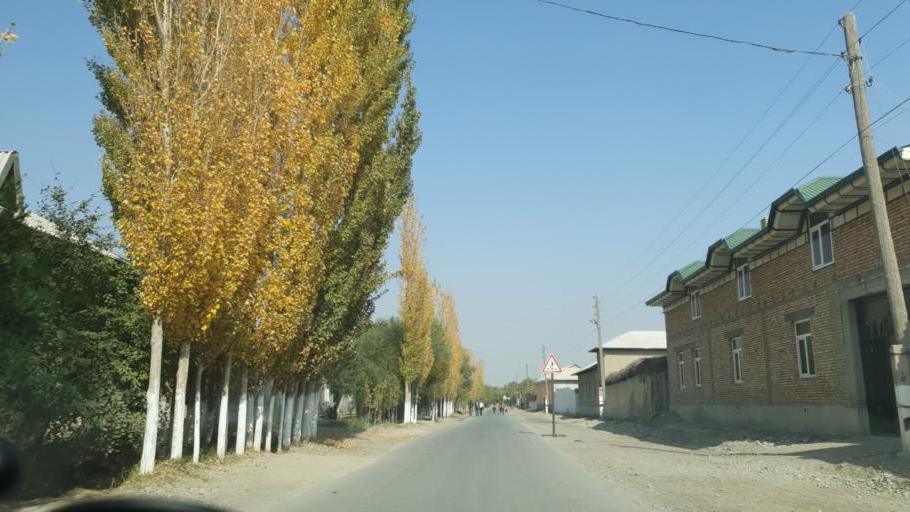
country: UZ
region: Fergana
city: Beshariq
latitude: 40.4928
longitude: 70.6211
